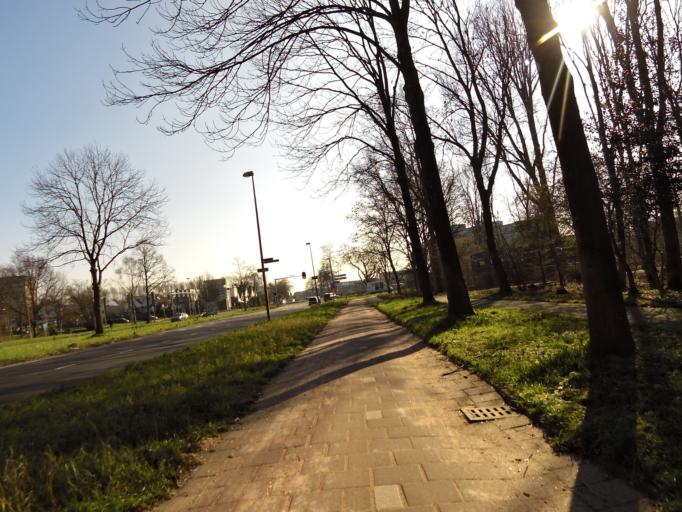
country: NL
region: South Holland
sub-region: Gemeente Leiderdorp
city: Leiderdorp
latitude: 52.1577
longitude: 4.5353
